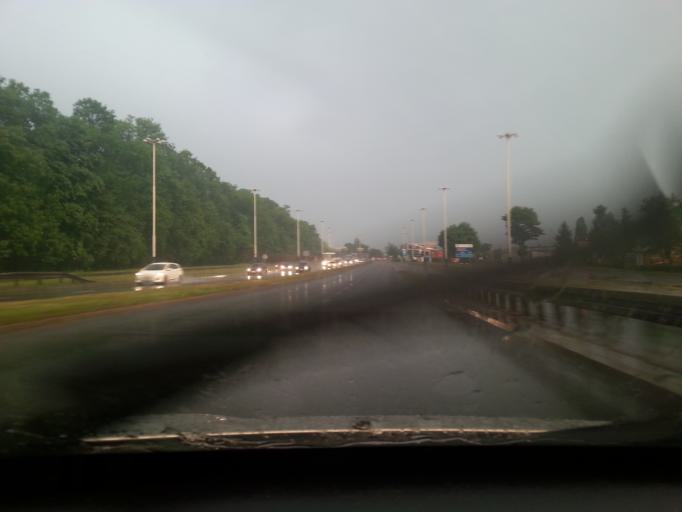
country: PL
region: Lodz Voivodeship
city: Lodz
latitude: 51.7543
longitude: 19.4354
